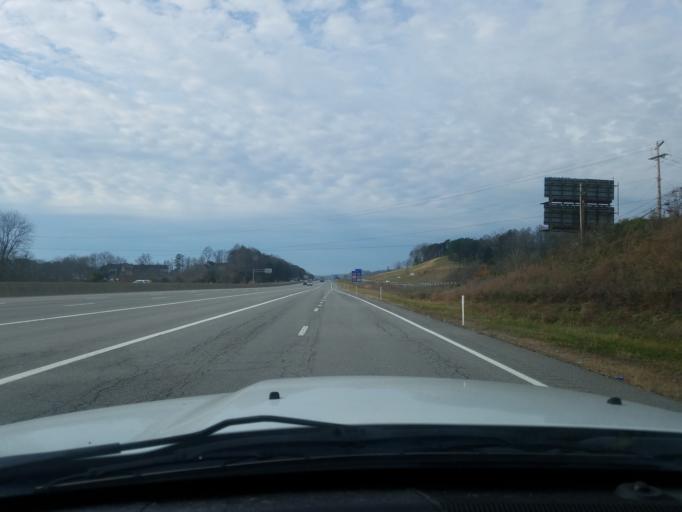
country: US
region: West Virginia
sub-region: Putnam County
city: Teays Valley
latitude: 38.4539
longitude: -81.9096
